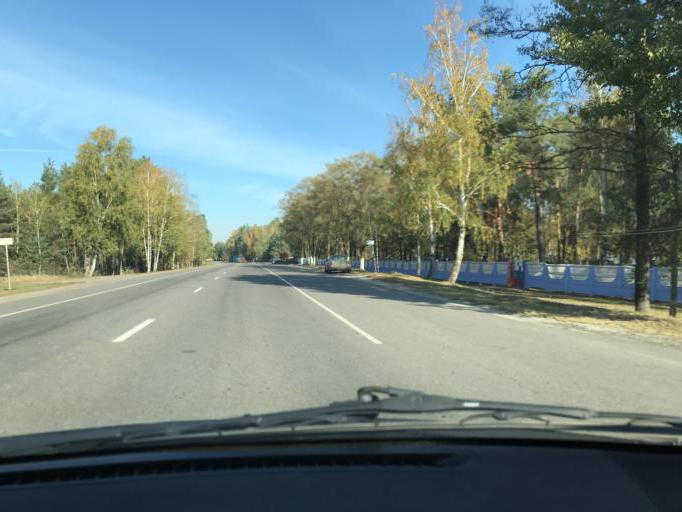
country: BY
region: Brest
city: Mikashevichy
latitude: 52.2354
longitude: 27.4486
